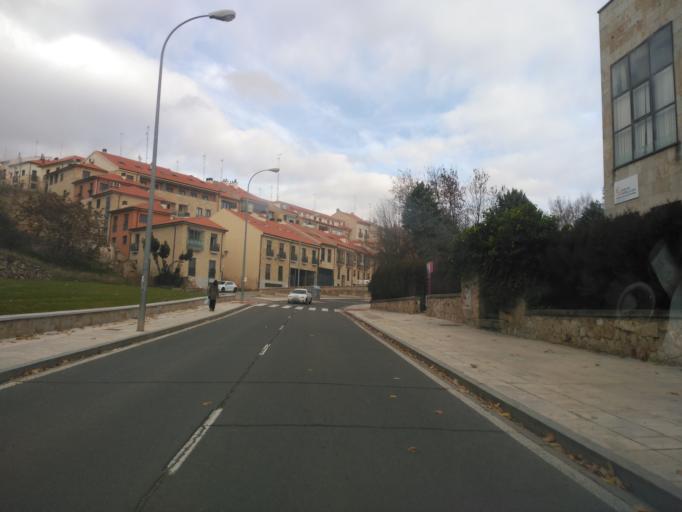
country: ES
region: Castille and Leon
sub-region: Provincia de Salamanca
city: Salamanca
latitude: 40.9613
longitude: -5.6724
